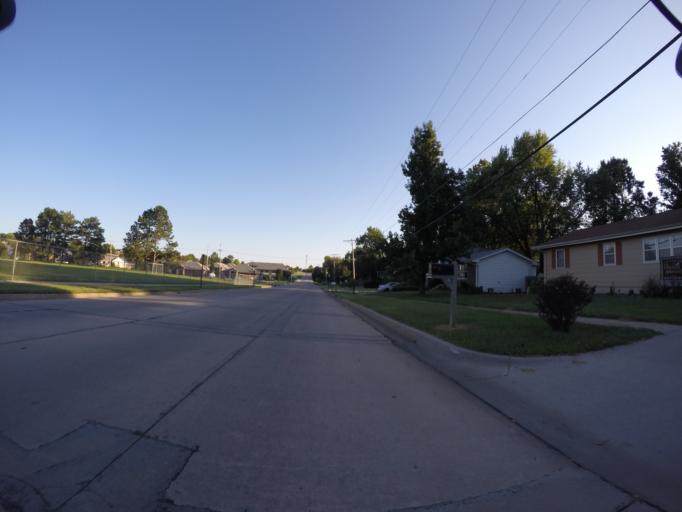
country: US
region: Kansas
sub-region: Riley County
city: Manhattan
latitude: 39.1972
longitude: -96.6076
